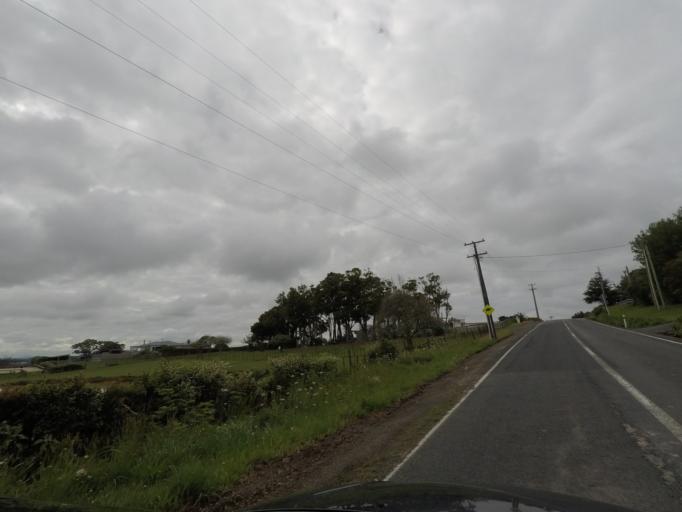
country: NZ
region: Auckland
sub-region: Auckland
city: Rosebank
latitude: -36.8026
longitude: 174.5740
